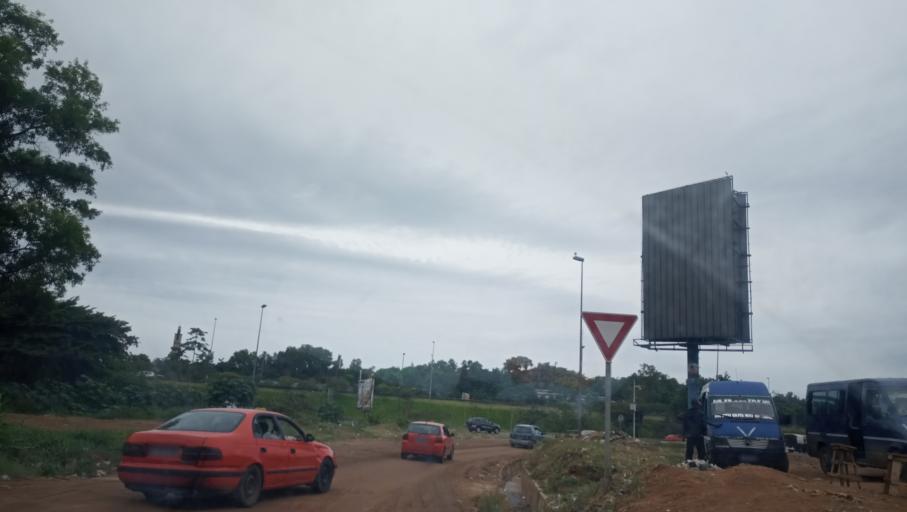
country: CI
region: Lagunes
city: Abidjan
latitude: 5.3536
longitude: -4.0118
